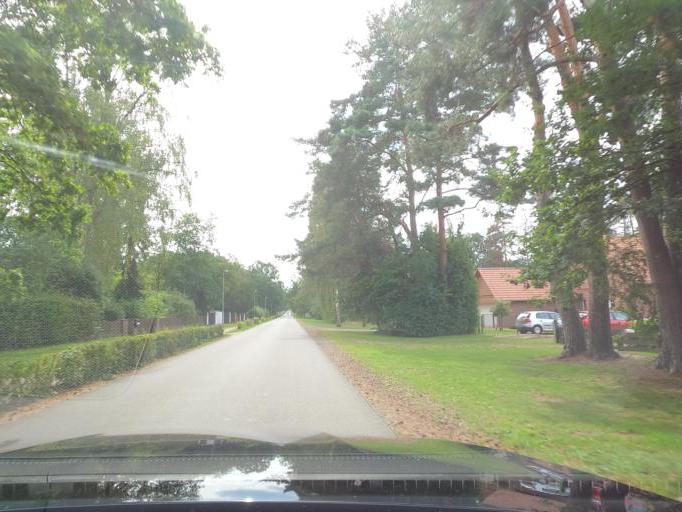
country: DE
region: Lower Saxony
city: Burgdorf
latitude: 52.5118
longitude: 9.9499
